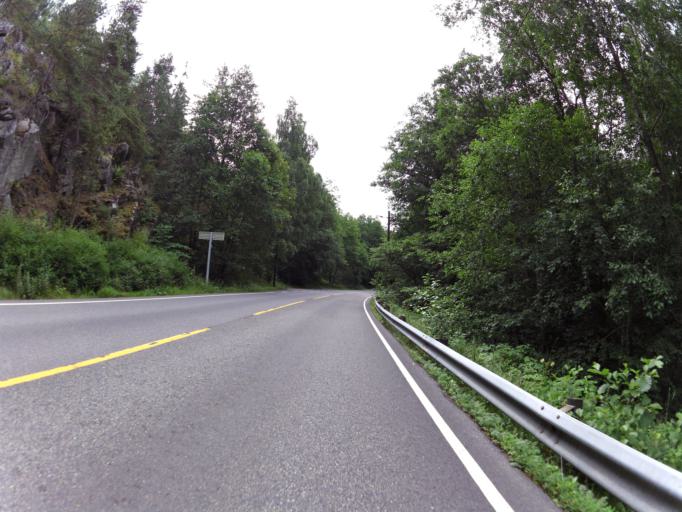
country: NO
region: Akershus
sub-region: Oppegard
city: Kolbotn
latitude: 59.8248
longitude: 10.7716
